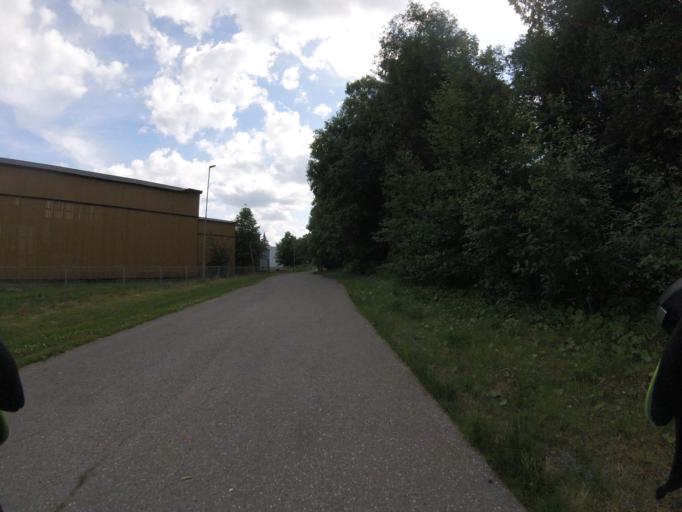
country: NO
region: Akershus
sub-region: Skedsmo
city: Lillestrom
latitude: 59.9537
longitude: 11.0227
